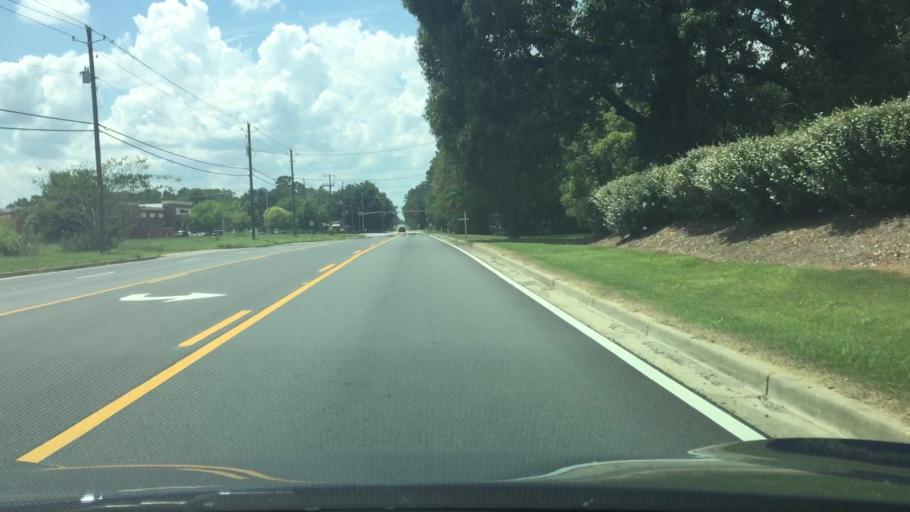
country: US
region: Alabama
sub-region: Montgomery County
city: Pike Road
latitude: 32.3494
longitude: -86.0951
